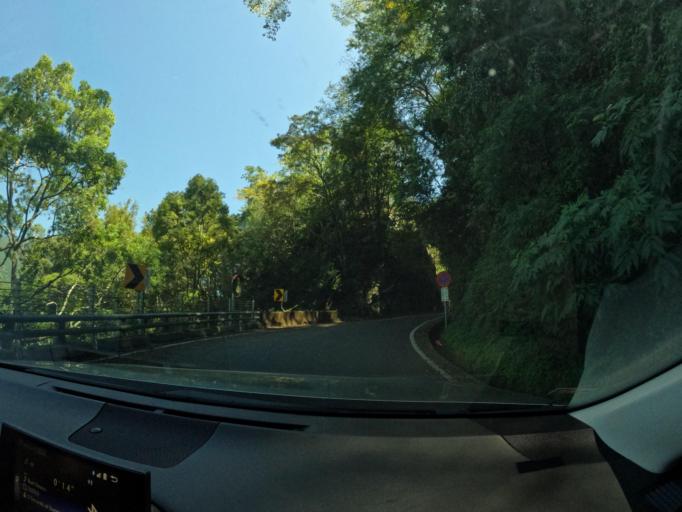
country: TW
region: Taiwan
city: Yujing
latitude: 23.2808
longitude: 120.8676
